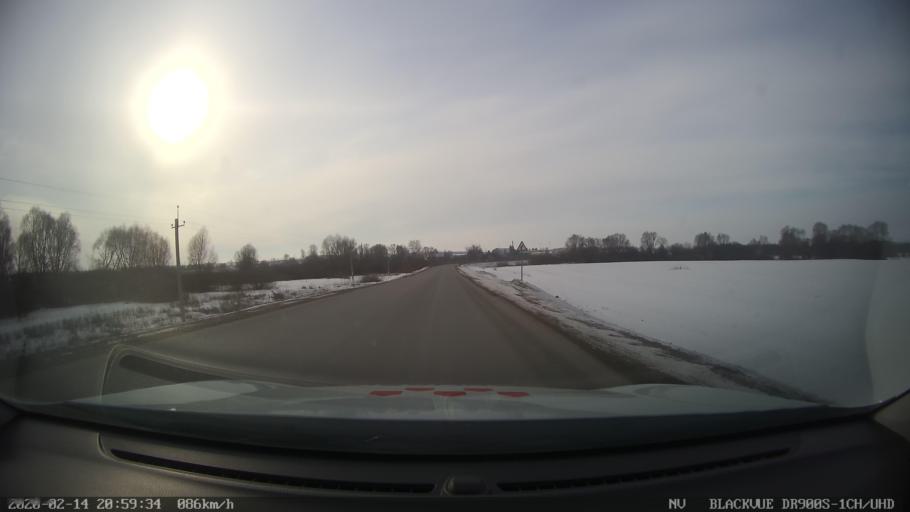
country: RU
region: Tatarstan
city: Kuybyshevskiy Zaton
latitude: 55.1775
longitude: 49.2365
